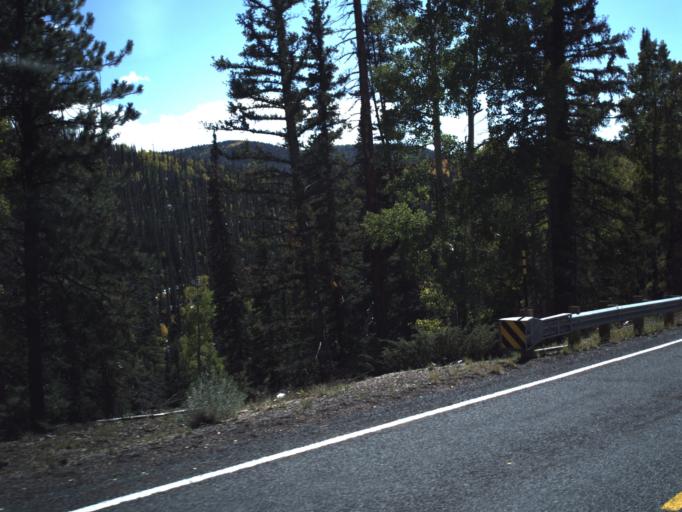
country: US
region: Utah
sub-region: Piute County
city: Junction
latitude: 38.3103
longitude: -112.4025
